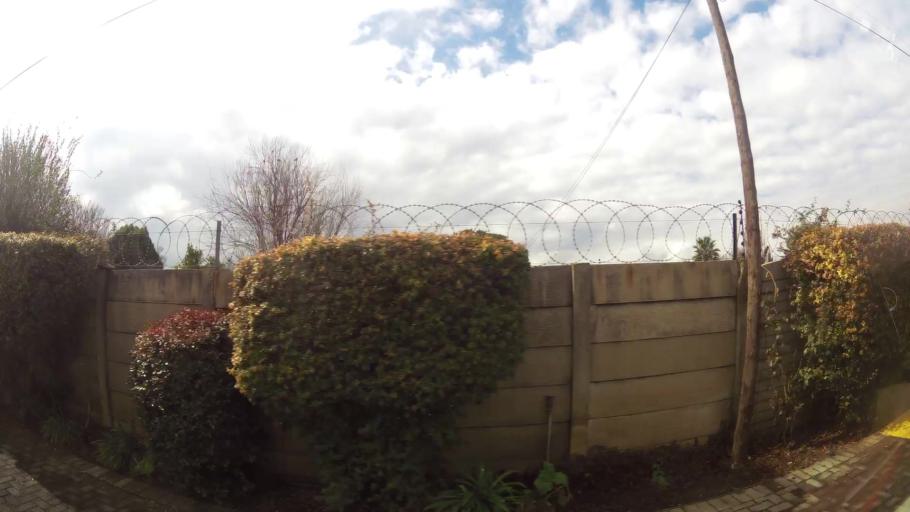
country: ZA
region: Gauteng
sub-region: Sedibeng District Municipality
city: Vereeniging
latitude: -26.6499
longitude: 27.9769
